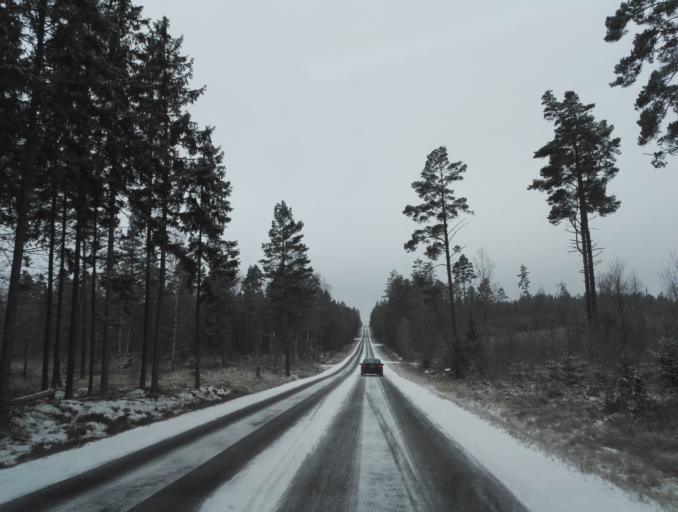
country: SE
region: Kronoberg
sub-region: Lessebo Kommun
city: Lessebo
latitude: 56.7670
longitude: 15.2934
